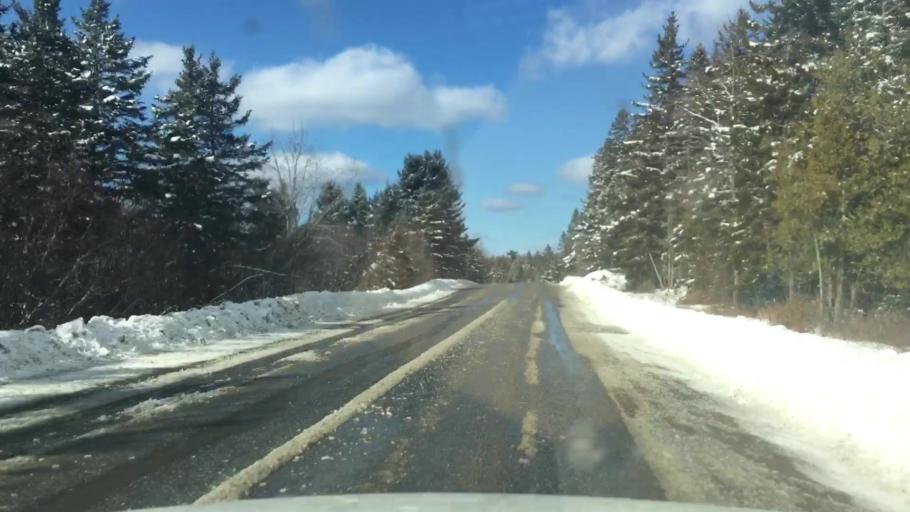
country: US
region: Maine
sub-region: Washington County
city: Machias
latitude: 44.6814
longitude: -67.4559
